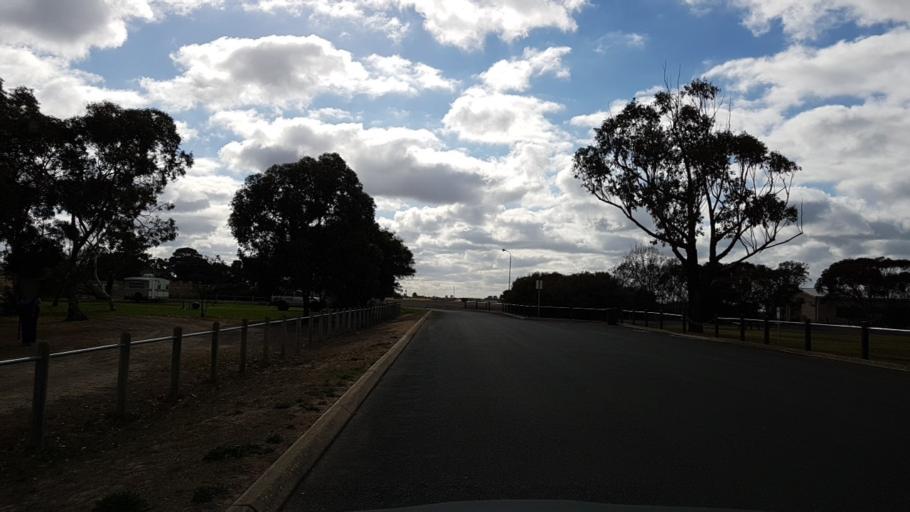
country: AU
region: South Australia
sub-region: Alexandrina
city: Langhorne Creek
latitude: -35.4063
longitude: 138.9761
